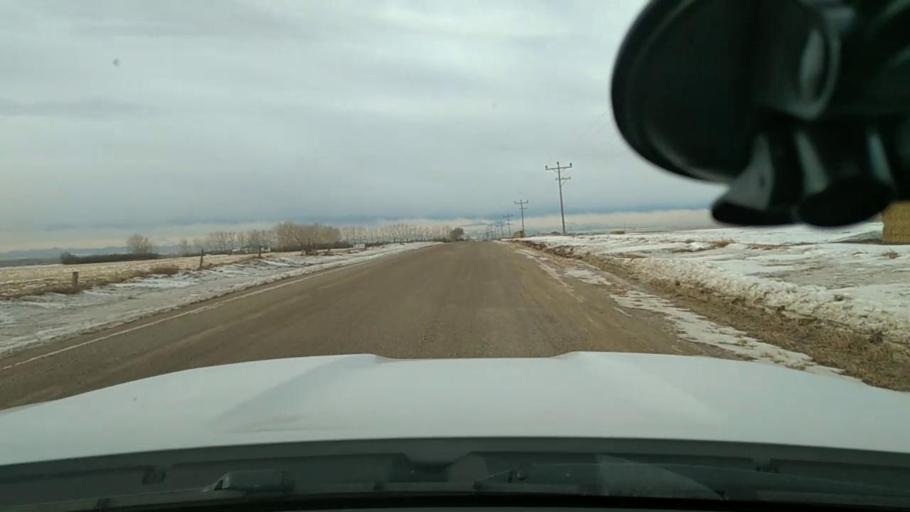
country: CA
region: Alberta
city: Airdrie
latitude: 51.2417
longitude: -113.9477
